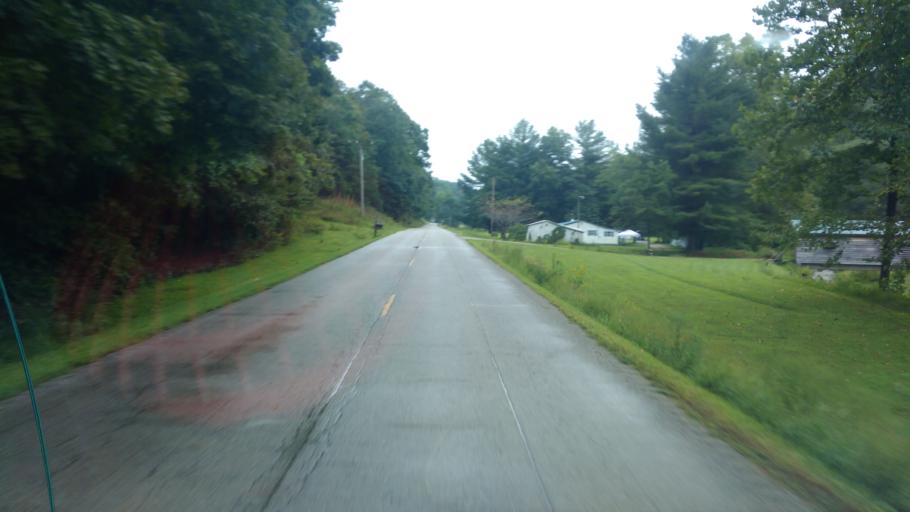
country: US
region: Kentucky
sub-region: Fleming County
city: Flemingsburg
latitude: 38.4491
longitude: -83.5106
